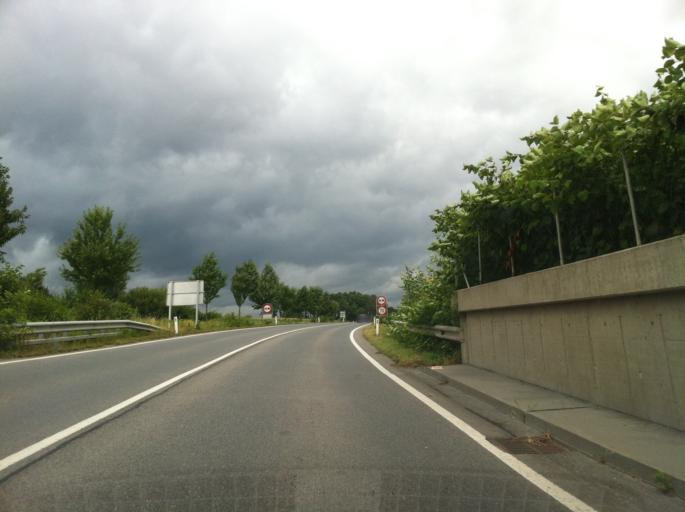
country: AT
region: Lower Austria
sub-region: Politischer Bezirk Tulln
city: Langenrohr
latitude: 48.2959
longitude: 16.0077
